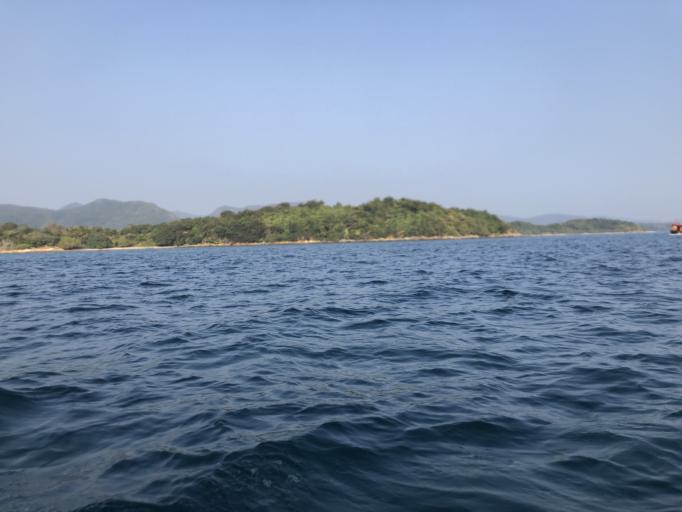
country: HK
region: Sai Kung
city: Sai Kung
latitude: 22.3779
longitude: 114.2783
